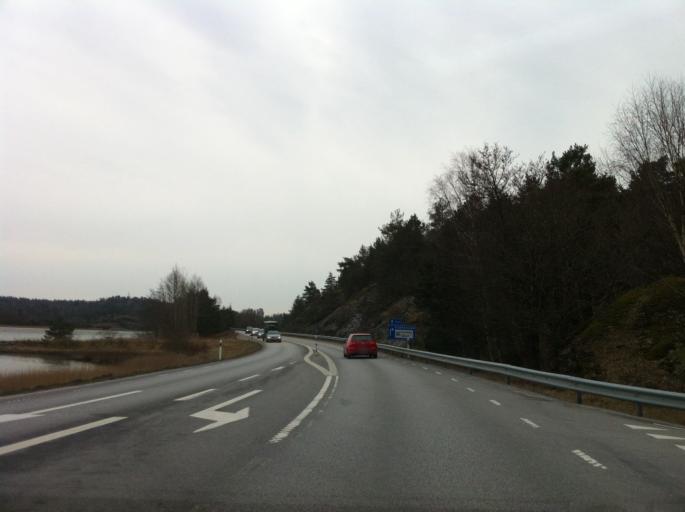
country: SE
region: Vaestra Goetaland
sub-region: Orust
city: Henan
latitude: 58.2745
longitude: 11.6938
